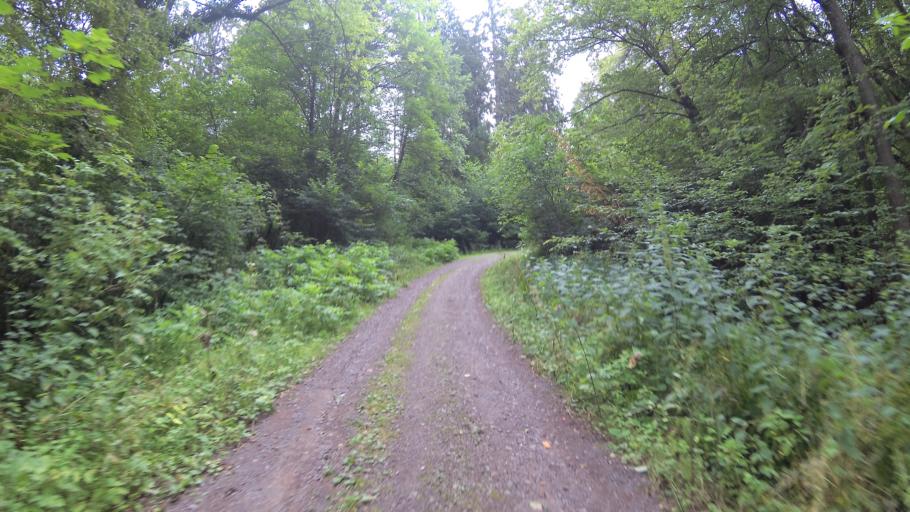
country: DE
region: Saarland
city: Mainzweiler
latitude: 49.4201
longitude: 7.1439
